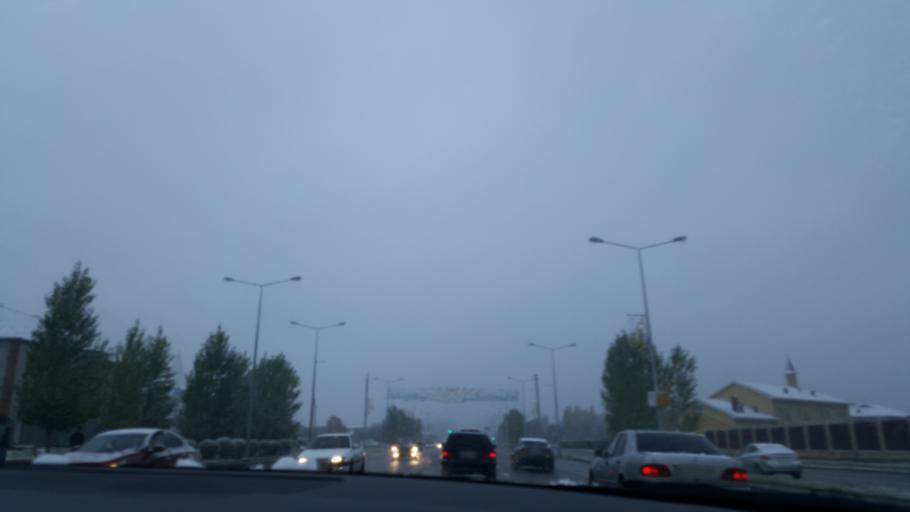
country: KZ
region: Astana Qalasy
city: Astana
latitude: 51.1461
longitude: 71.4997
